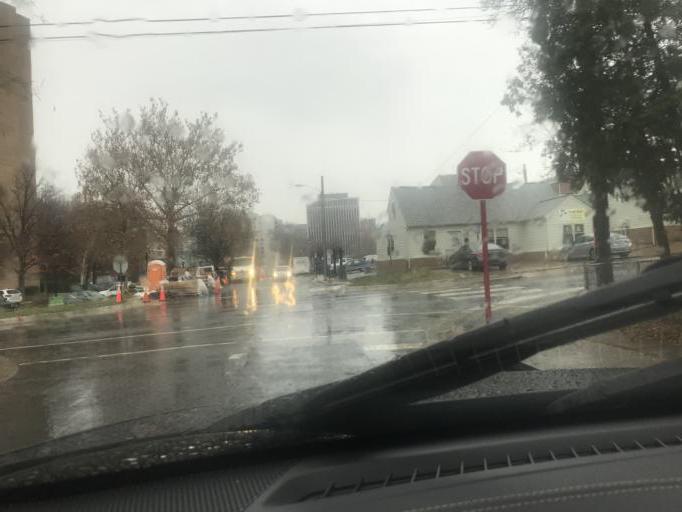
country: US
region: Washington, D.C.
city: Washington, D.C.
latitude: 38.8541
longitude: -77.0556
